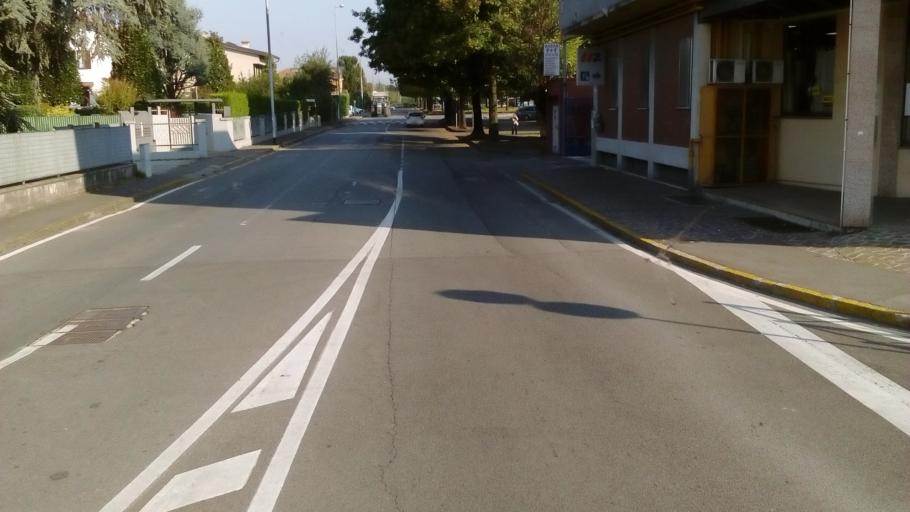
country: IT
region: Lombardy
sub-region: Provincia di Bergamo
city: Treviglio
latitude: 45.5276
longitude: 9.5854
